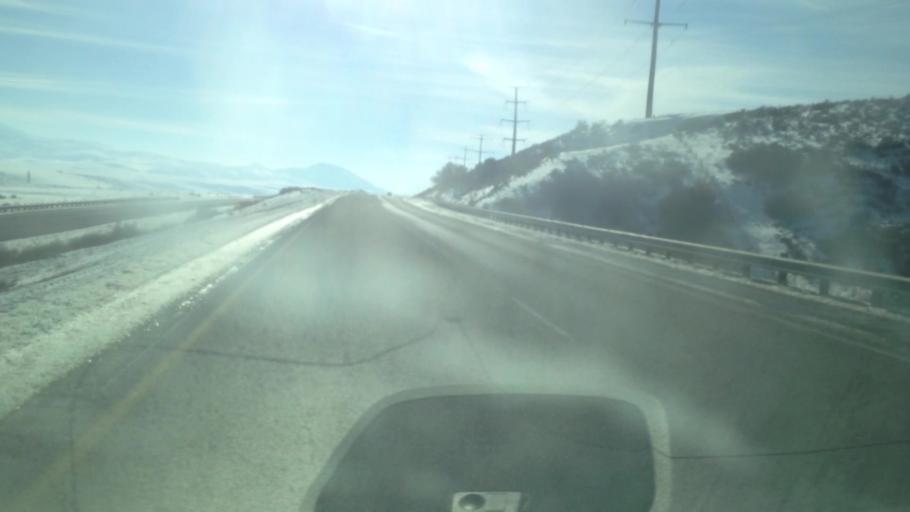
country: US
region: Idaho
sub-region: Oneida County
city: Malad City
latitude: 42.2776
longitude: -112.2117
